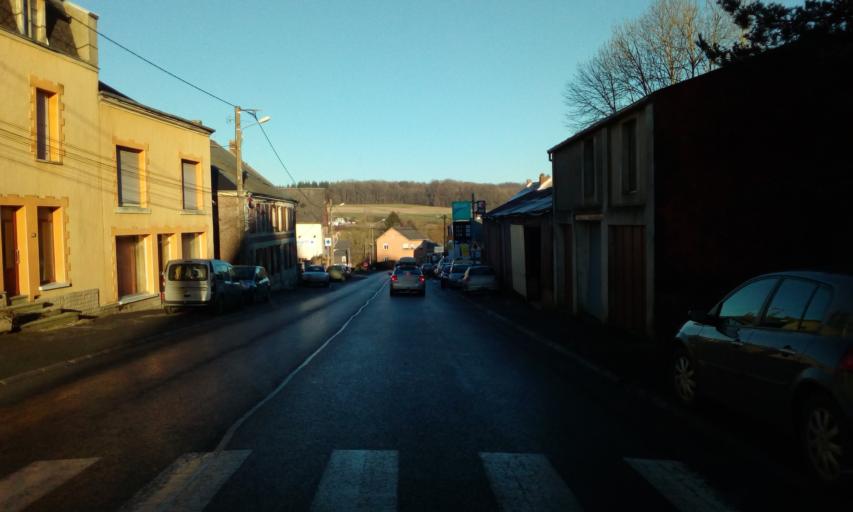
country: FR
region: Champagne-Ardenne
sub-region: Departement des Ardennes
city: Signy-le-Petit
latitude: 49.7700
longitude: 4.3406
